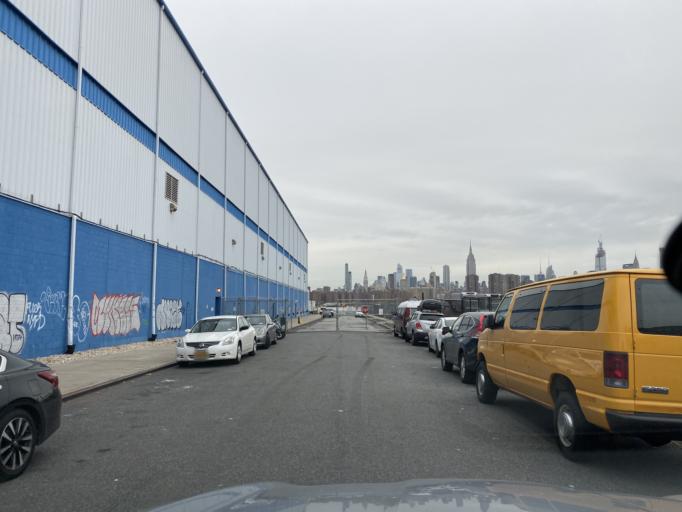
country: US
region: New York
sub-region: Queens County
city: Long Island City
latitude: 40.7231
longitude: -73.9602
